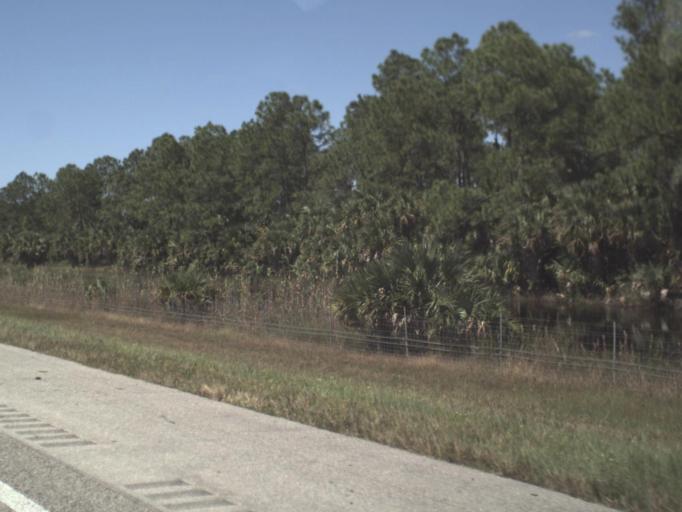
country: US
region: Florida
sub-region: Collier County
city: Golden Gate
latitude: 26.1532
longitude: -81.5576
